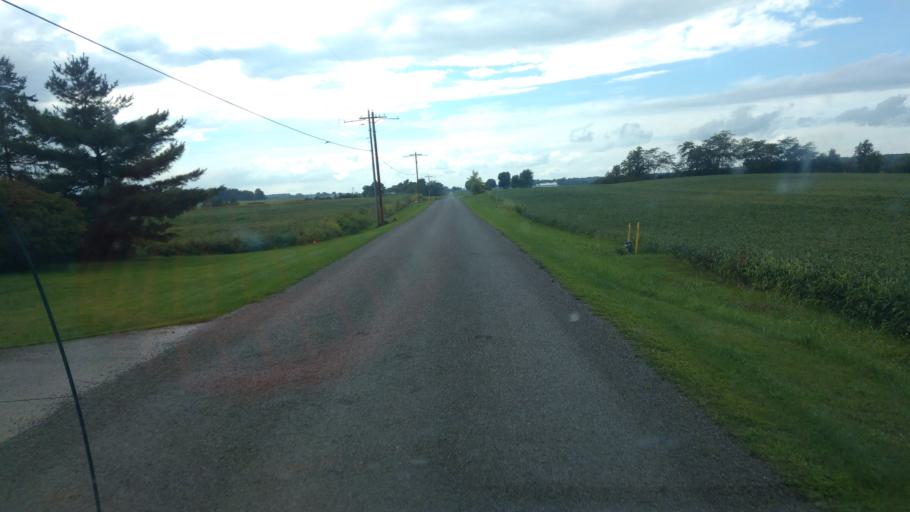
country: US
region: Ohio
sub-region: Hardin County
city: Kenton
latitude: 40.7038
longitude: -83.6266
